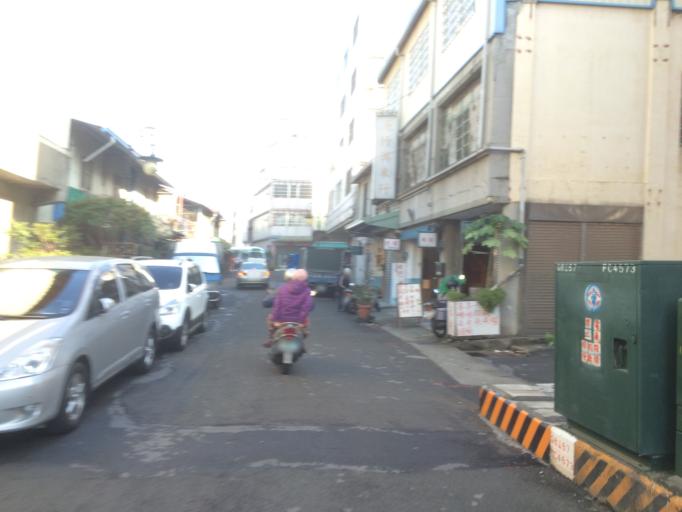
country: TW
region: Taiwan
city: Fengyuan
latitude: 24.2121
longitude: 120.7063
